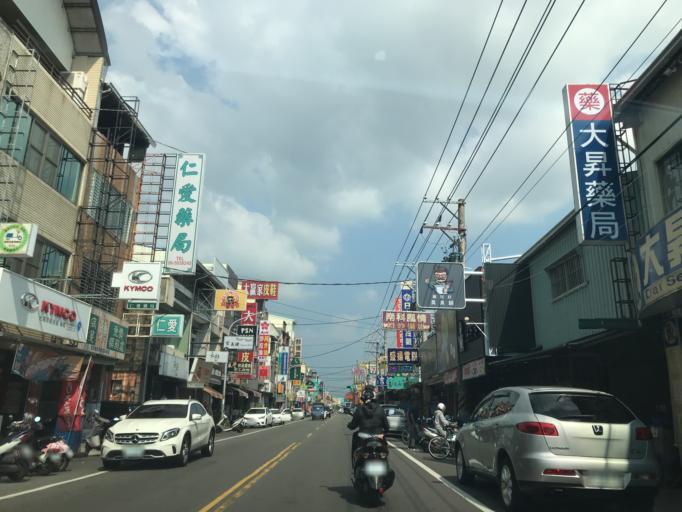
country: TW
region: Taiwan
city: Yujing
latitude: 23.1326
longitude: 120.3003
